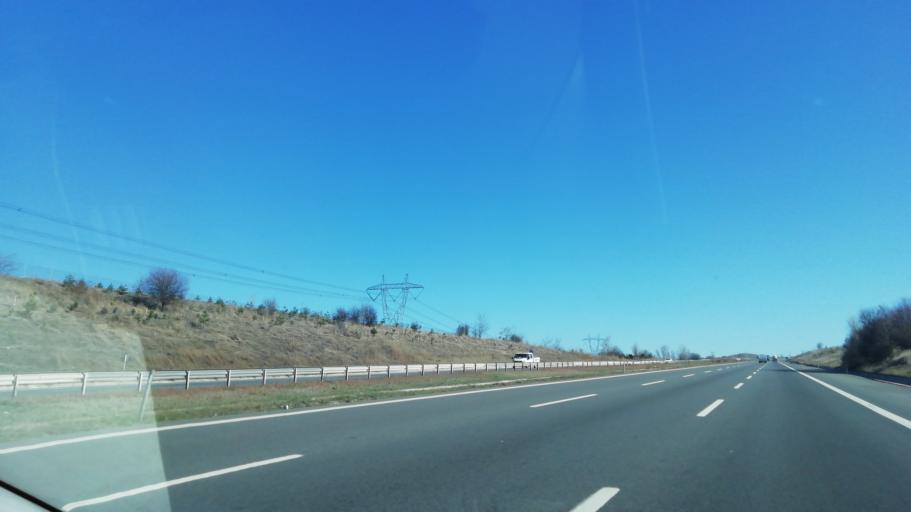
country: TR
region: Bolu
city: Yenicaga
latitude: 40.7646
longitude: 32.0448
